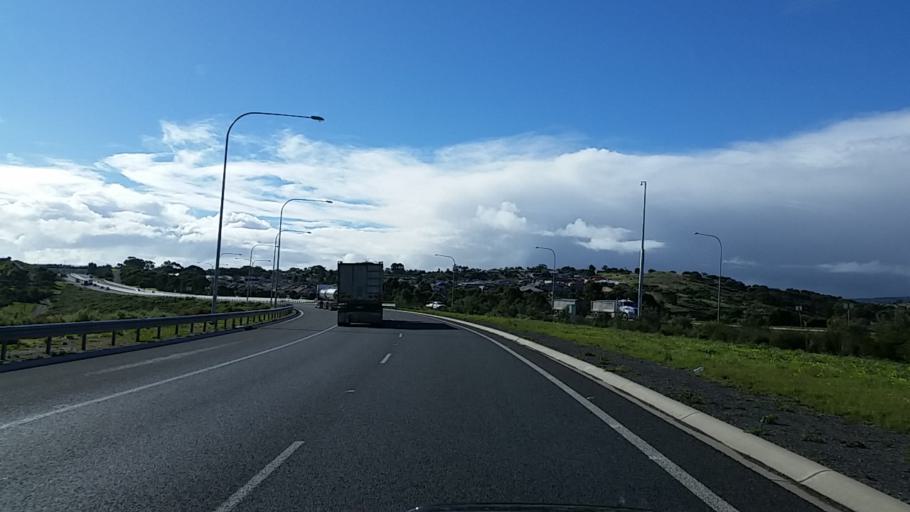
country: AU
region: South Australia
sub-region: Onkaparinga
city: Noarlunga Downs
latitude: -35.1658
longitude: 138.5079
